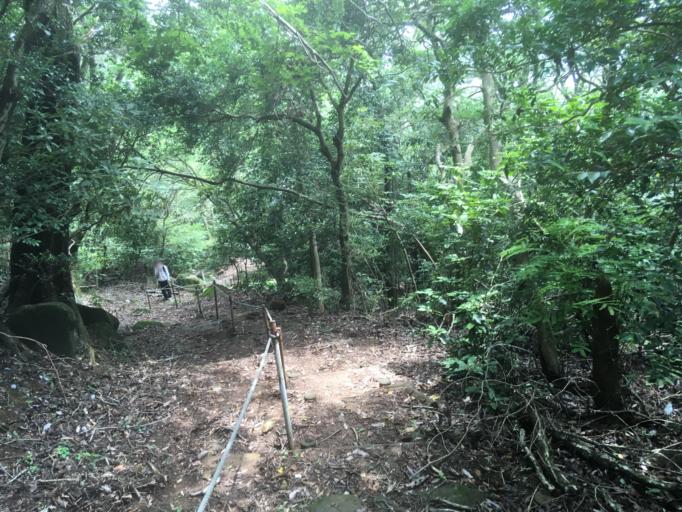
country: JP
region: Nara
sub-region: Ikoma-shi
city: Ikoma
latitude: 34.6764
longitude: 135.6807
